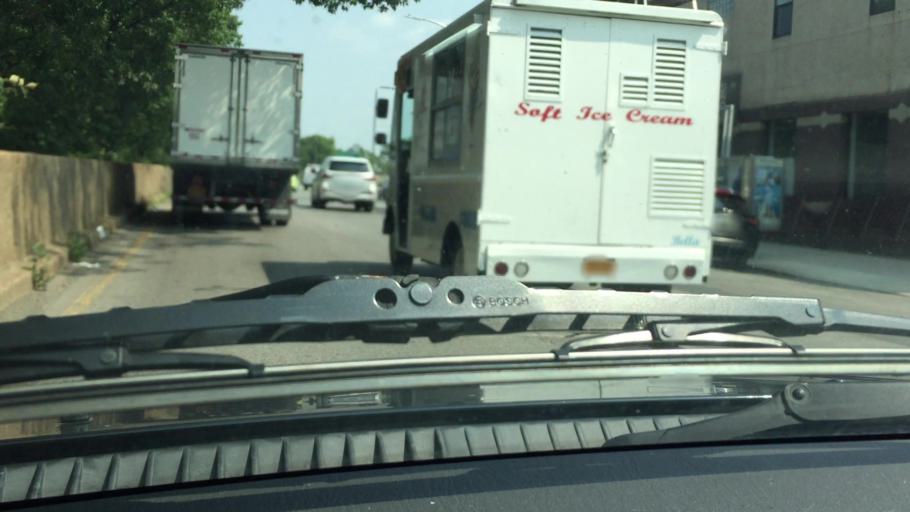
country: US
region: New York
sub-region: Queens County
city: Long Island City
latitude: 40.7682
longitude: -73.9067
